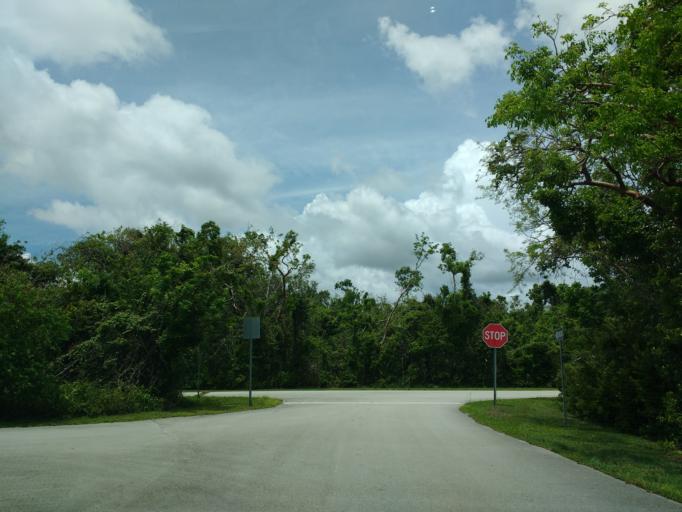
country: US
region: Florida
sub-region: Miami-Dade County
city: Florida City
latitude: 25.3837
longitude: -80.6102
